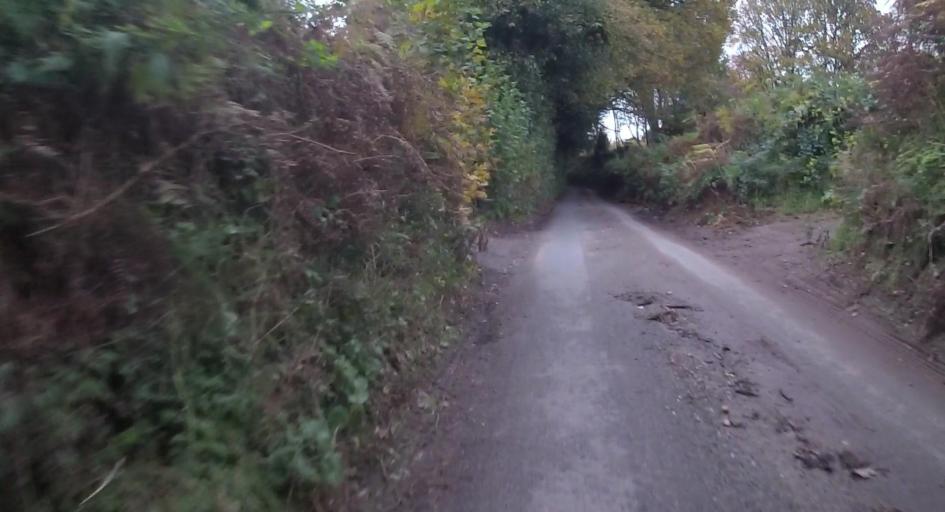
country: GB
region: England
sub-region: Surrey
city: Churt
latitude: 51.1345
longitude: -0.7972
